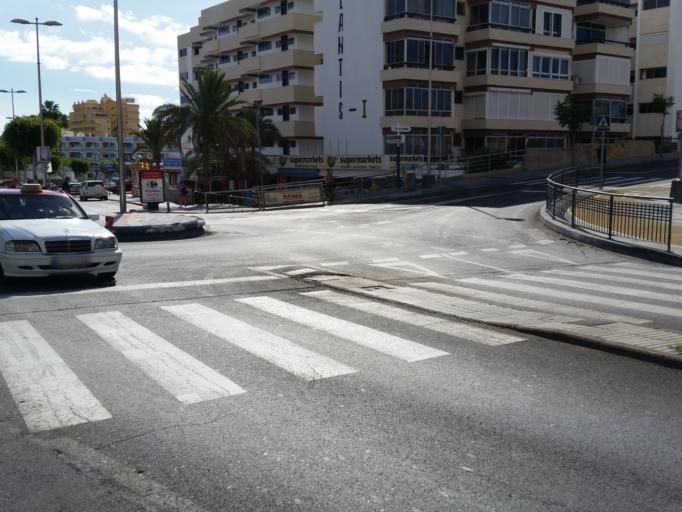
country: ES
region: Canary Islands
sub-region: Provincia de Las Palmas
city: Playa del Ingles
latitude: 27.7593
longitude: -15.5747
